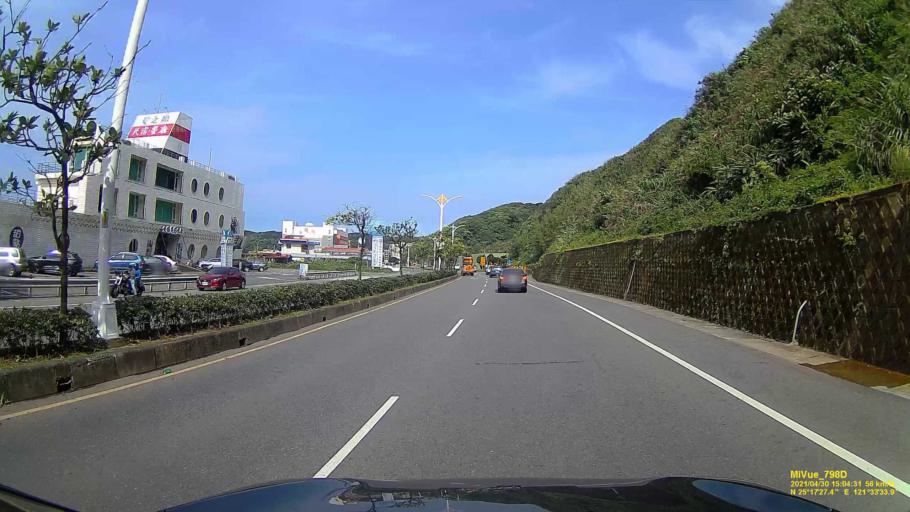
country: TW
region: Taiwan
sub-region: Keelung
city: Keelung
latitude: 25.2909
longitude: 121.5597
